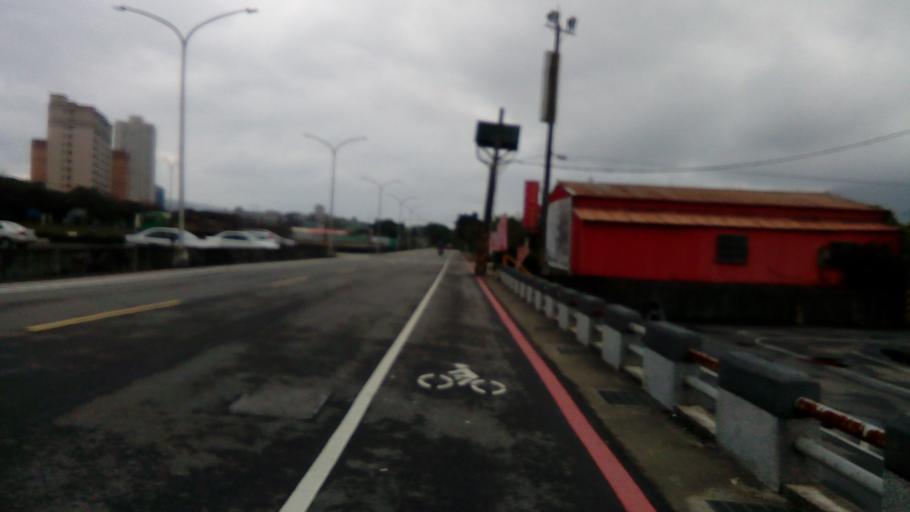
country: TW
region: Taipei
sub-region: Taipei
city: Banqiao
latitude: 25.1807
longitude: 121.4193
